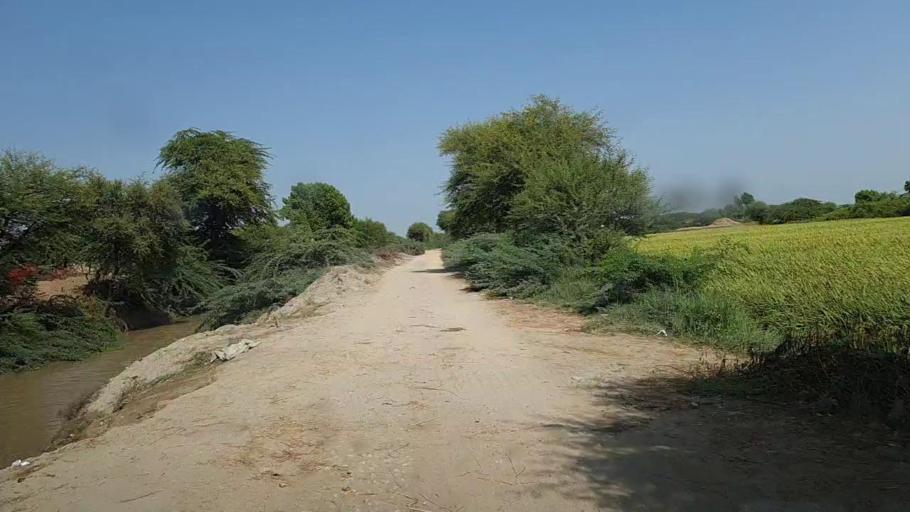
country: PK
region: Sindh
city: Mirpur Batoro
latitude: 24.7144
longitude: 68.4375
